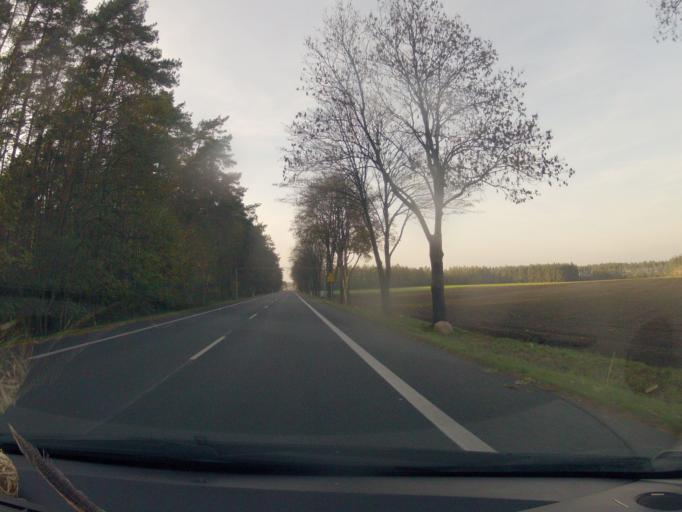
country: PL
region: Opole Voivodeship
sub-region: Powiat strzelecki
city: Strzelce Opolskie
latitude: 50.5456
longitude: 18.2354
